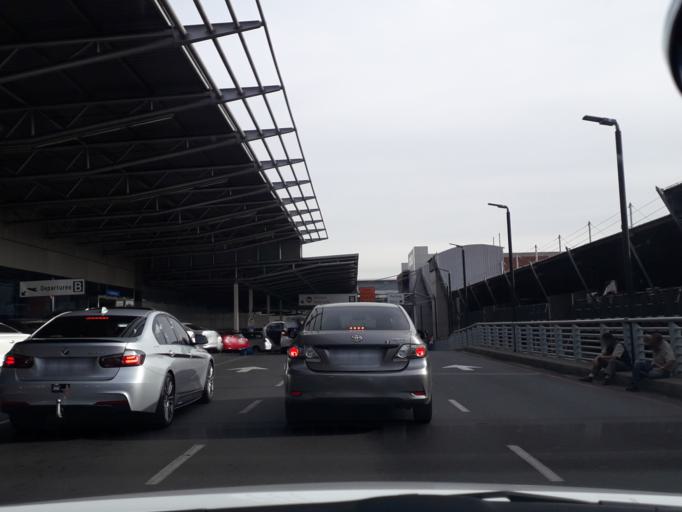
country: ZA
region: Gauteng
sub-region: City of Johannesburg Metropolitan Municipality
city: Modderfontein
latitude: -26.1343
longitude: 28.2313
